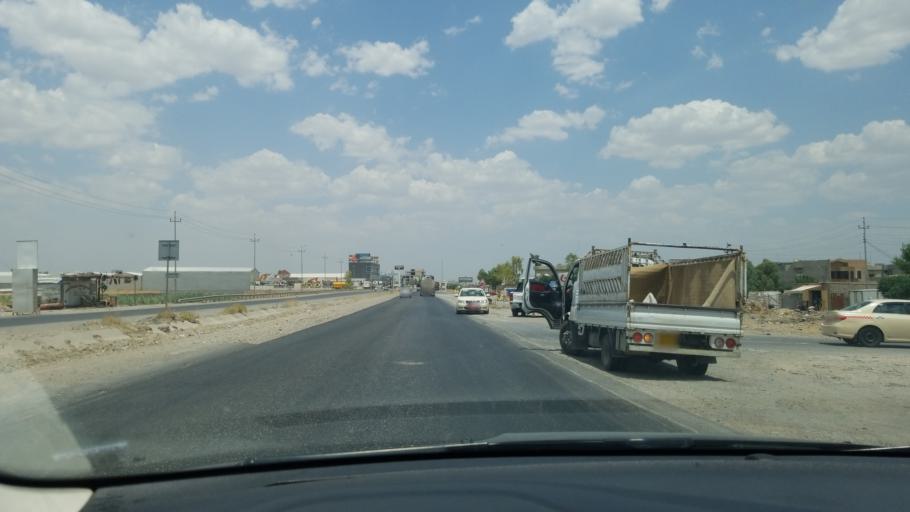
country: IQ
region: Arbil
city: Erbil
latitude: 36.0968
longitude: 44.0215
